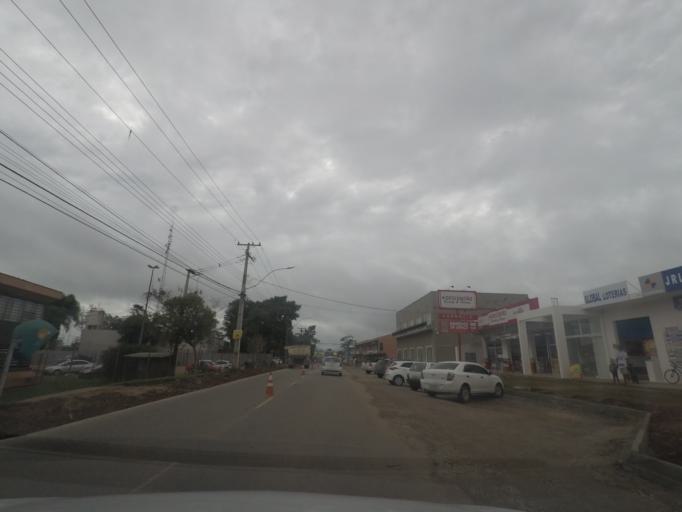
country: BR
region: Parana
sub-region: Piraquara
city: Piraquara
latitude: -25.4521
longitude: -49.0700
